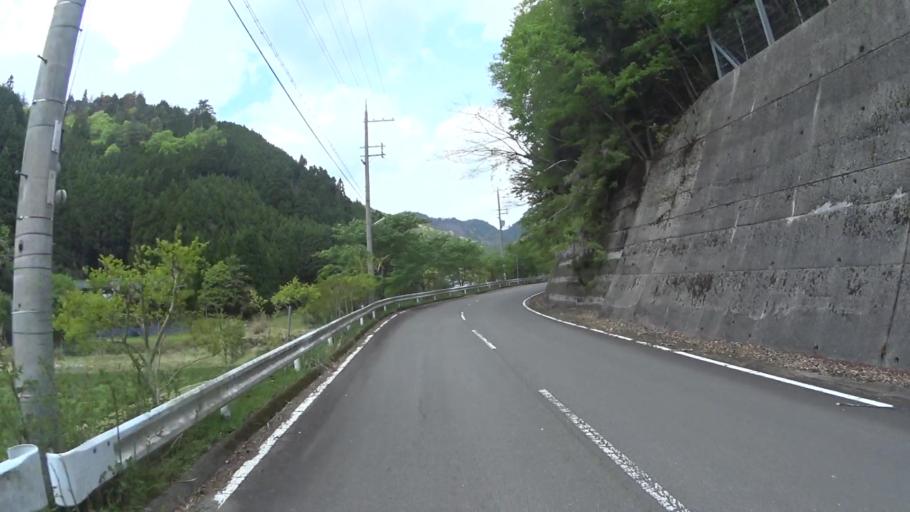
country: JP
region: Kyoto
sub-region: Kyoto-shi
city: Kamigyo-ku
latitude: 35.1190
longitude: 135.7038
